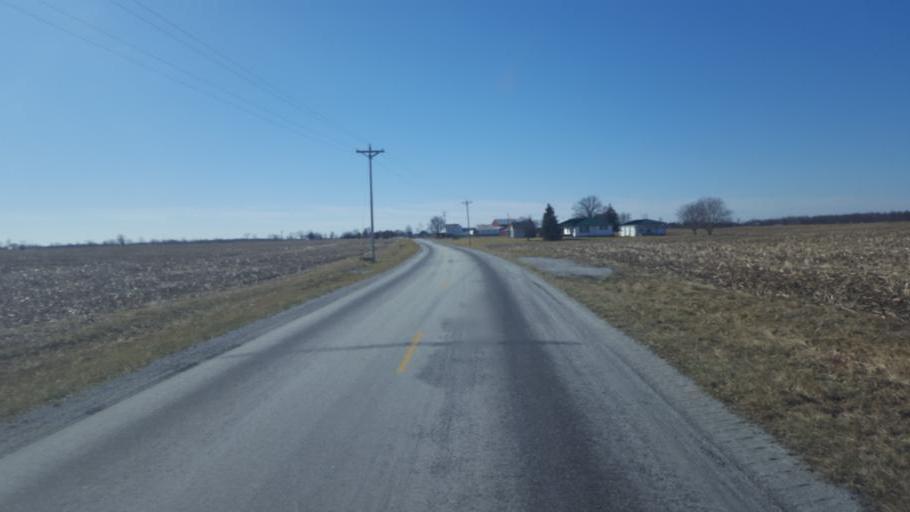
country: US
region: Ohio
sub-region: Hardin County
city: Kenton
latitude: 40.6341
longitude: -83.4837
